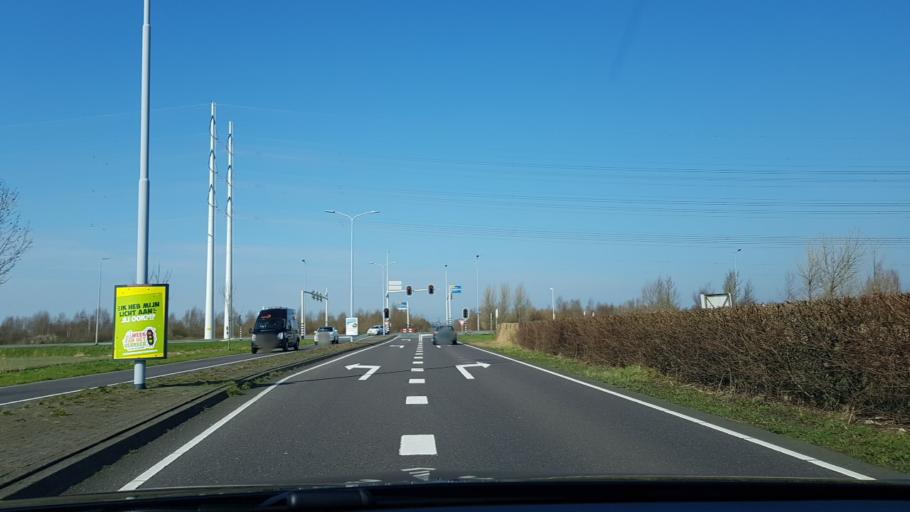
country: NL
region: South Holland
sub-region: Gemeente Hillegom
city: Hillegom
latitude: 52.2894
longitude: 4.6148
